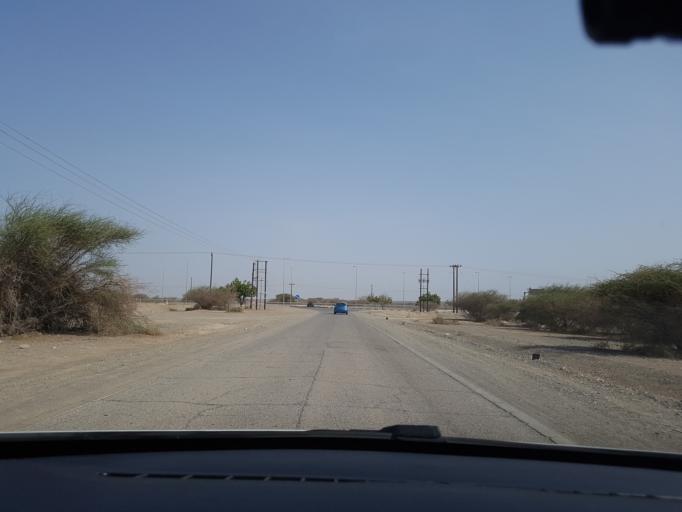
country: OM
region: Al Batinah
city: Al Liwa'
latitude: 24.4035
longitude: 56.5815
